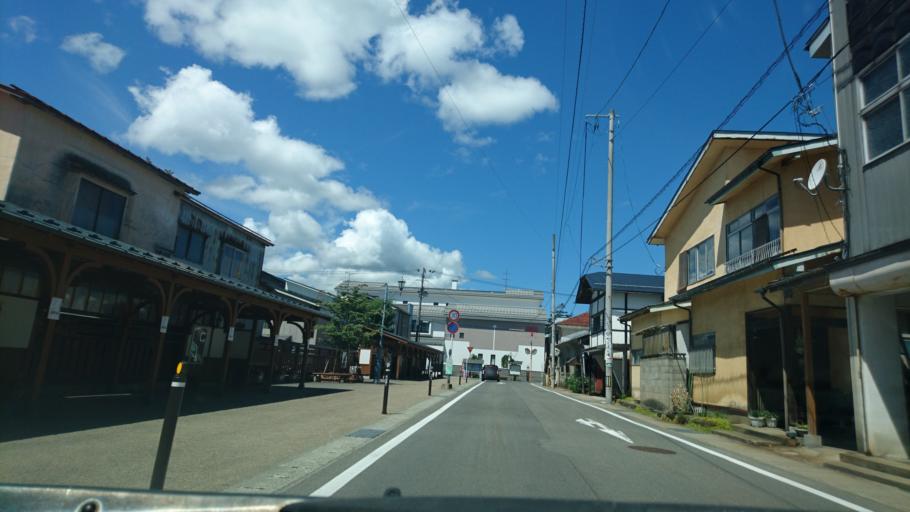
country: JP
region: Akita
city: Kakunodatemachi
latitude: 39.5937
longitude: 140.5636
